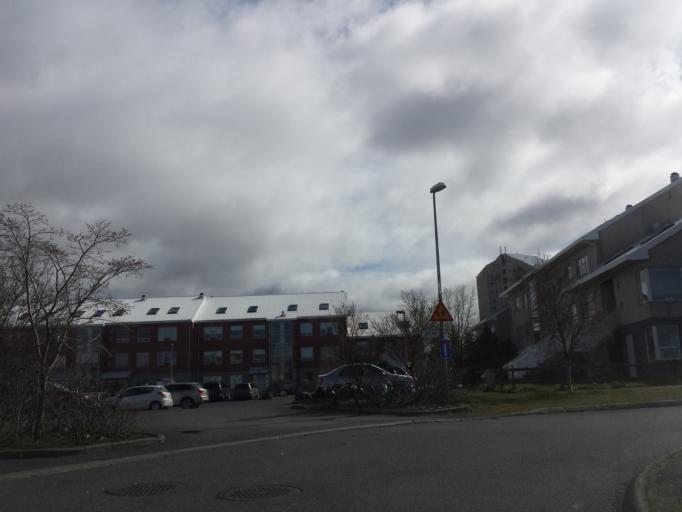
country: IS
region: Capital Region
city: Kopavogur
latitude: 64.1036
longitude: -21.8893
